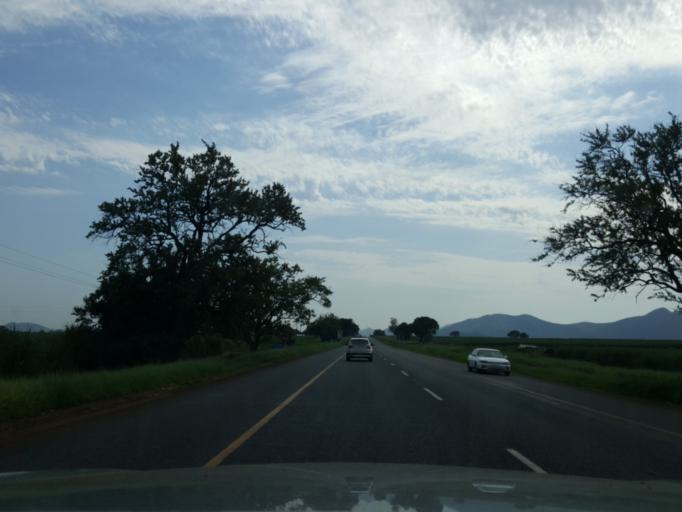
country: SZ
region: Hhohho
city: Ntfonjeni
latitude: -25.5075
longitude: 31.4851
